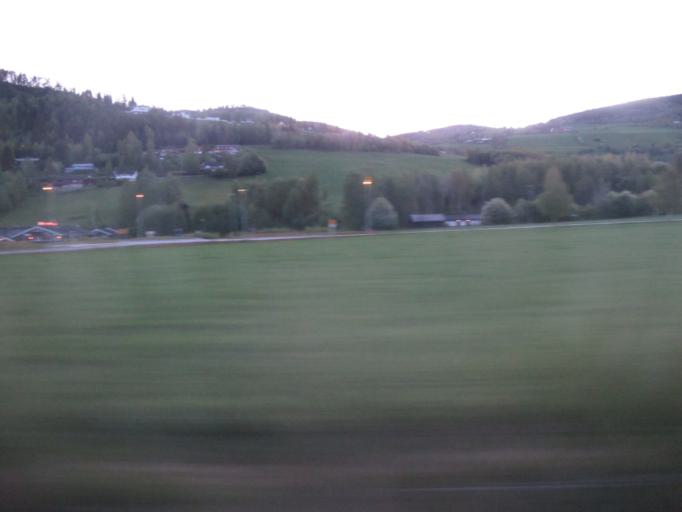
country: NO
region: Oppland
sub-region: Nord-Fron
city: Vinstra
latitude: 61.5880
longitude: 9.7699
